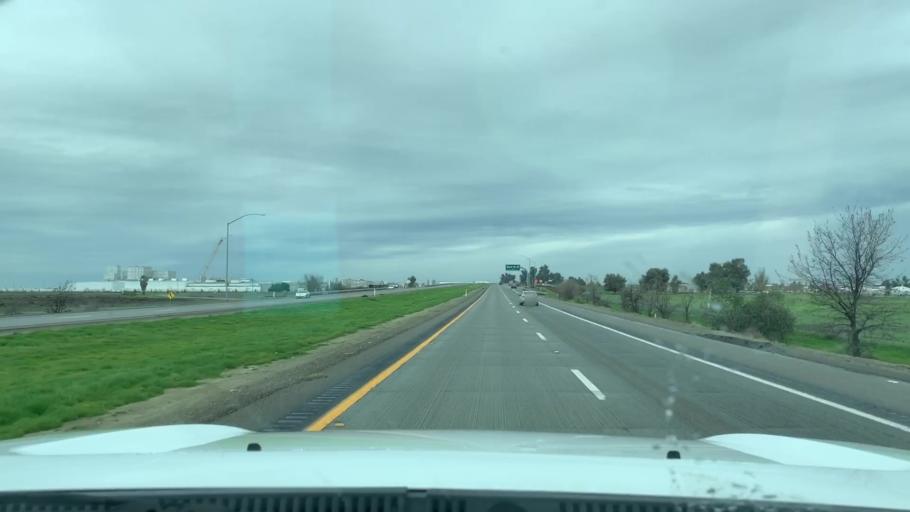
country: US
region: California
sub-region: Kings County
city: Lemoore
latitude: 36.2912
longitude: -119.8086
